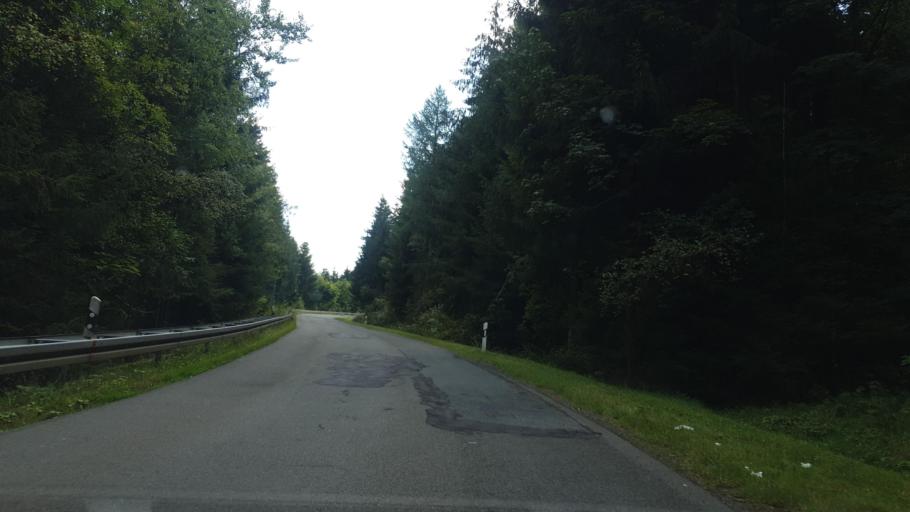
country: DE
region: Saxony
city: Eibenstock
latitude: 50.5031
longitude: 12.5783
